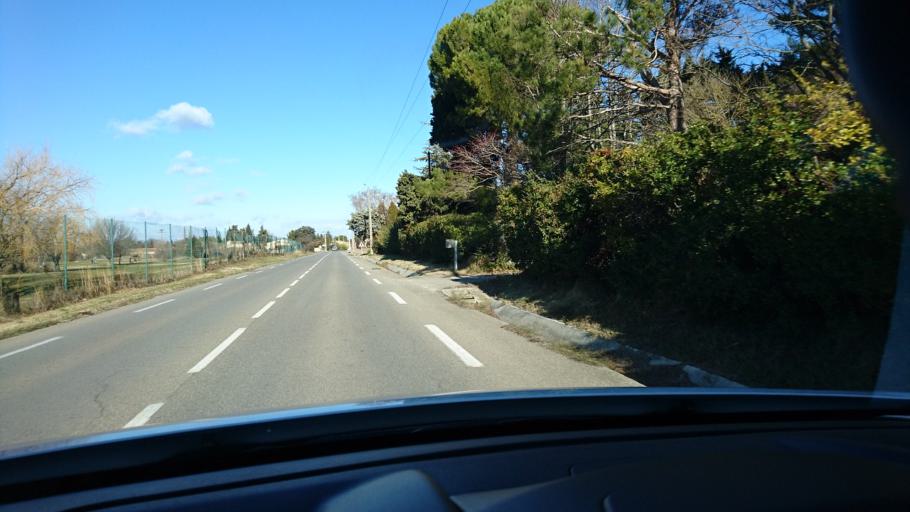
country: FR
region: Provence-Alpes-Cote d'Azur
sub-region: Departement du Vaucluse
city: Morieres-les-Avignon
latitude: 43.9228
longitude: 4.9054
